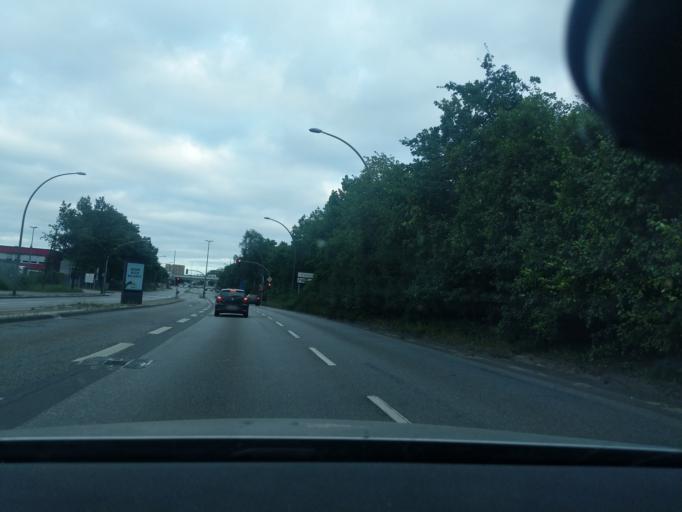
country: DE
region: Hamburg
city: Stellingen
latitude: 53.5841
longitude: 9.9097
